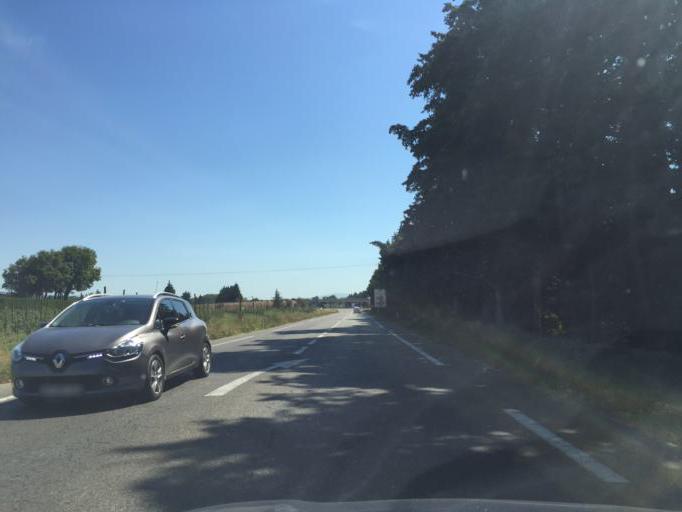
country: FR
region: Provence-Alpes-Cote d'Azur
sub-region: Departement du Vaucluse
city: L'Isle-sur-la-Sorgue
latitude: 43.8769
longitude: 5.0346
